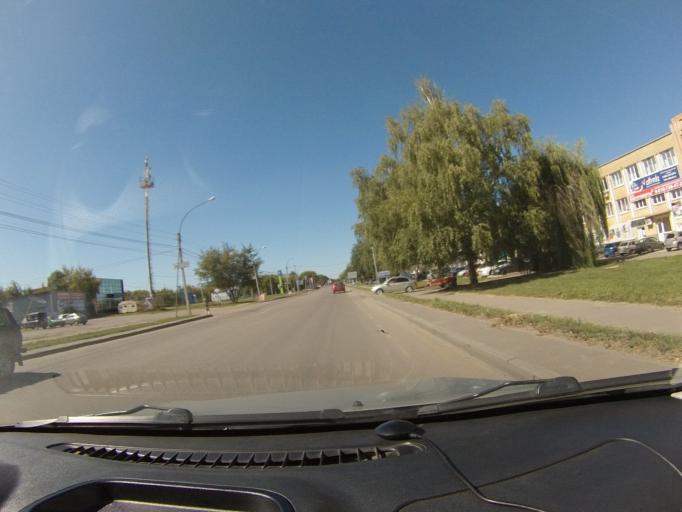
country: RU
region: Tambov
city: Donskoye
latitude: 52.7580
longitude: 41.4687
